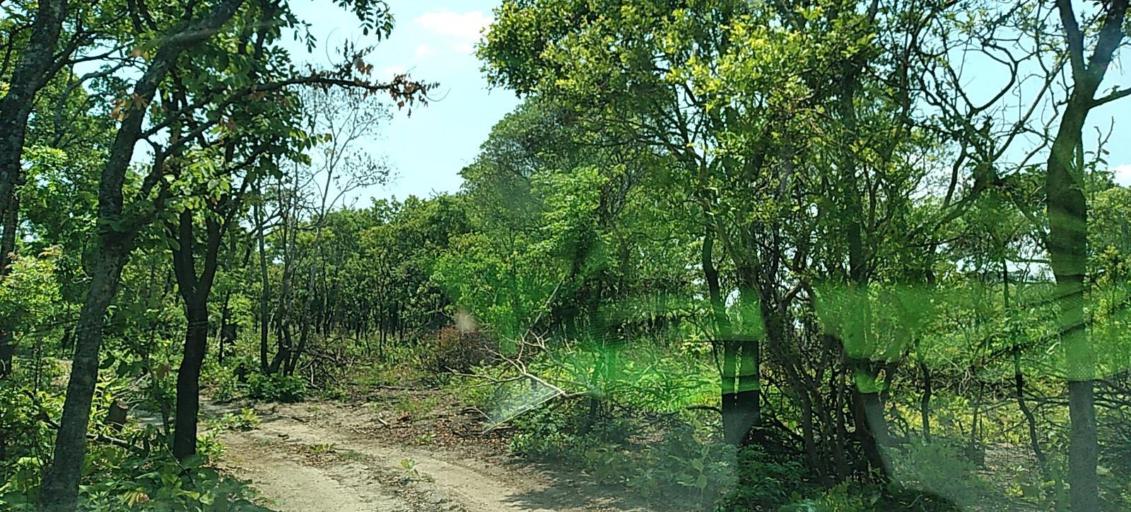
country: CD
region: Katanga
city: Kolwezi
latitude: -11.3021
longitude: 25.2311
